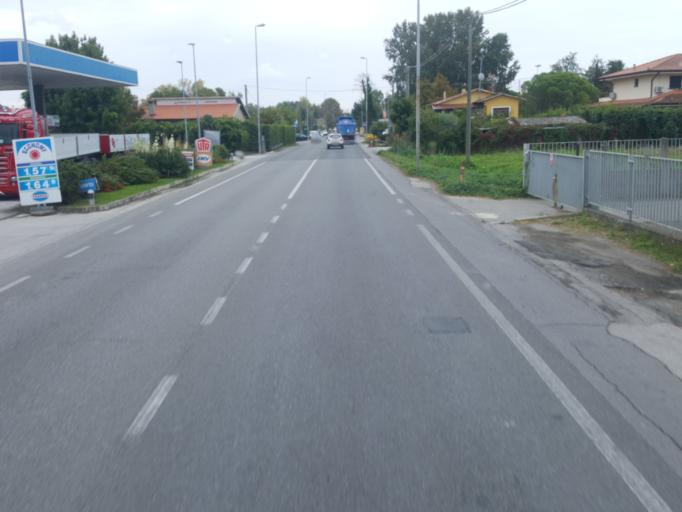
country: IT
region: Tuscany
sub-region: Provincia di Lucca
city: Forte dei Marmi
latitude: 43.9653
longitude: 10.1860
